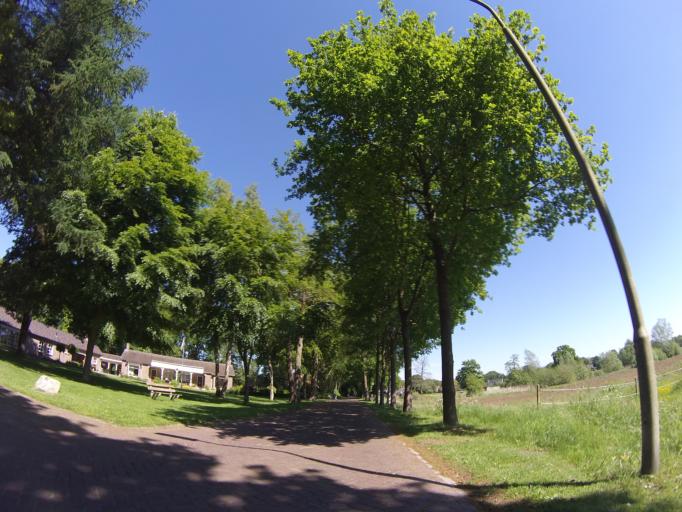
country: NL
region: Drenthe
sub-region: Gemeente Coevorden
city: Sleen
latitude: 52.7890
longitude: 6.7256
